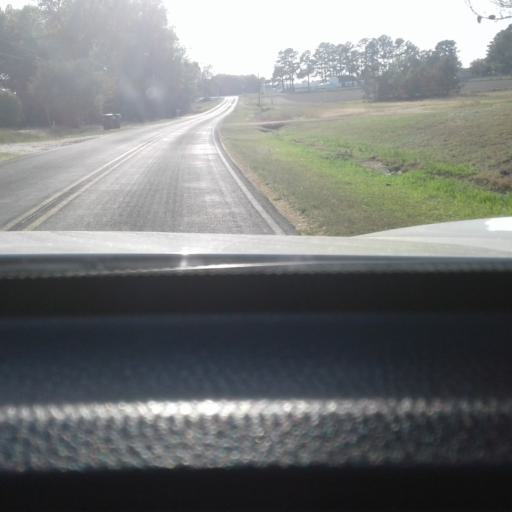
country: US
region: North Carolina
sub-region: Harnett County
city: Dunn
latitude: 35.3349
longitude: -78.5839
